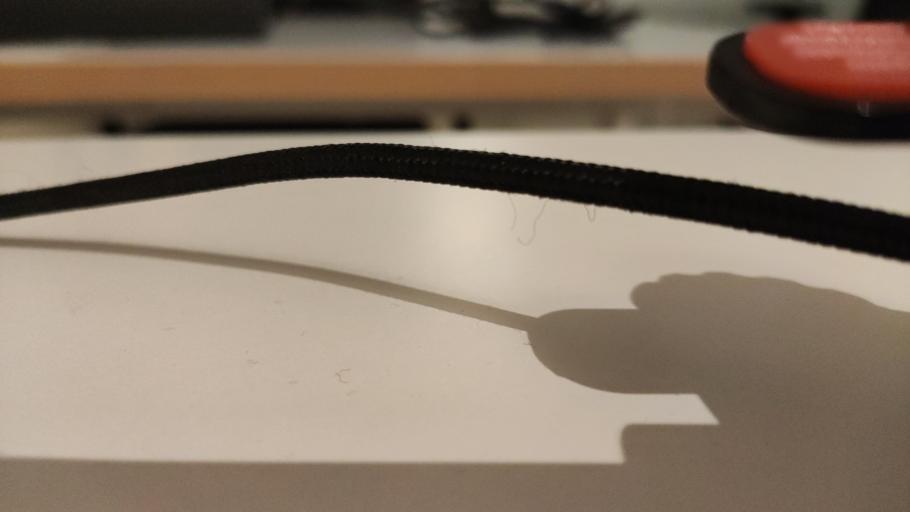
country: RU
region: Moskovskaya
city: Bogorodskoye
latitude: 56.4412
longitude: 37.8997
